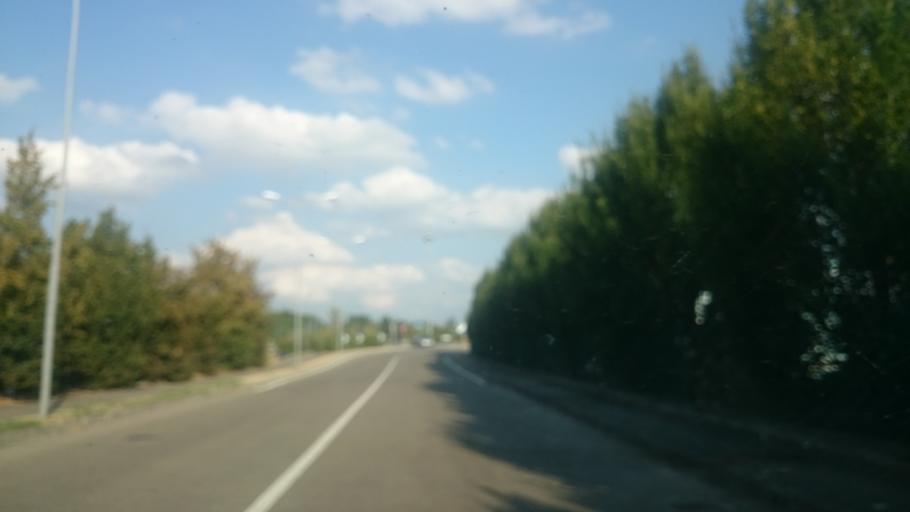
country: IT
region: Emilia-Romagna
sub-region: Provincia di Reggio Emilia
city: Rubiera
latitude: 44.6408
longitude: 10.7739
